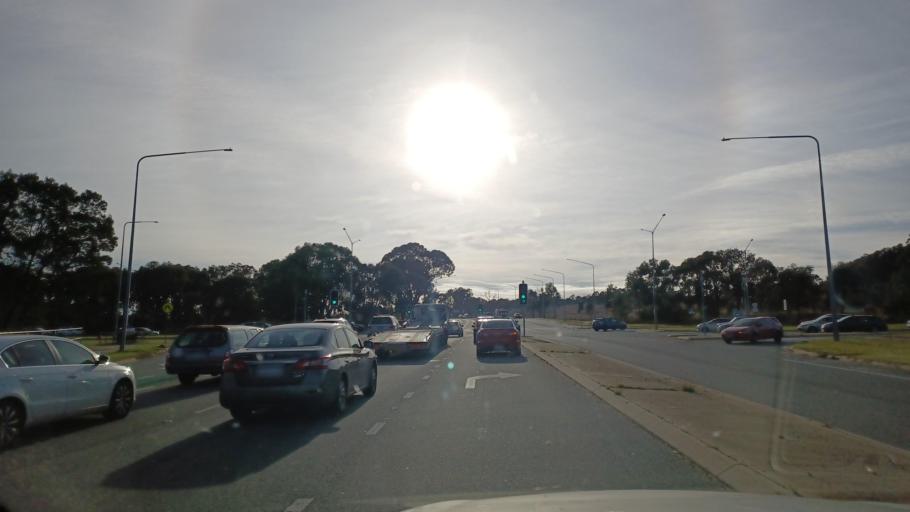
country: AU
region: Australian Capital Territory
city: Belconnen
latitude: -35.1845
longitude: 149.0749
